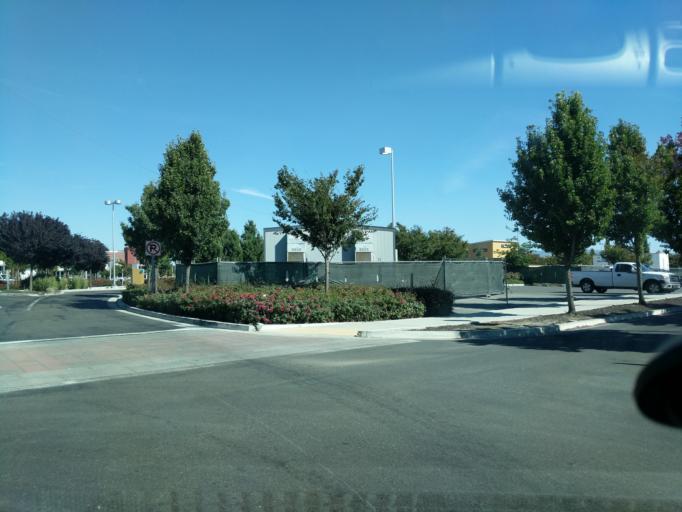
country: US
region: California
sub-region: Alameda County
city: Pleasanton
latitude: 37.7056
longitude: -121.8529
